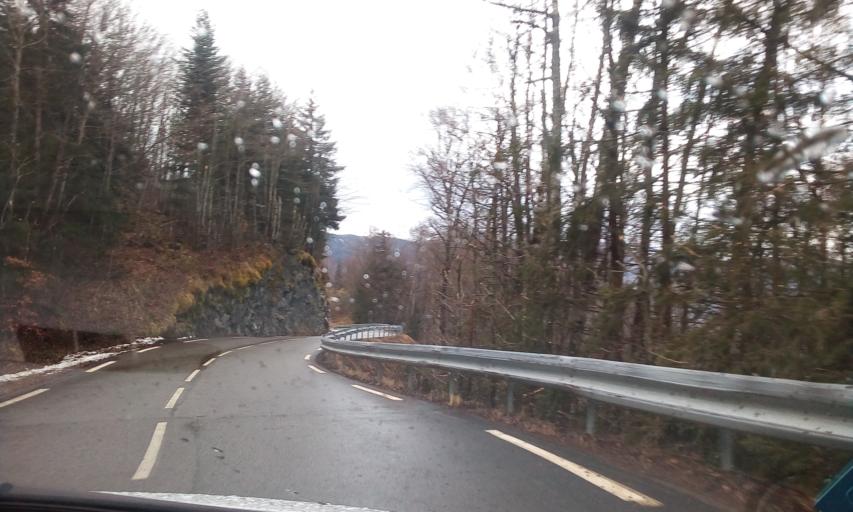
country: FR
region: Rhone-Alpes
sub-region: Departement de l'Isere
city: Vaulnaveys-le-Bas
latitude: 45.0471
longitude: 5.8491
